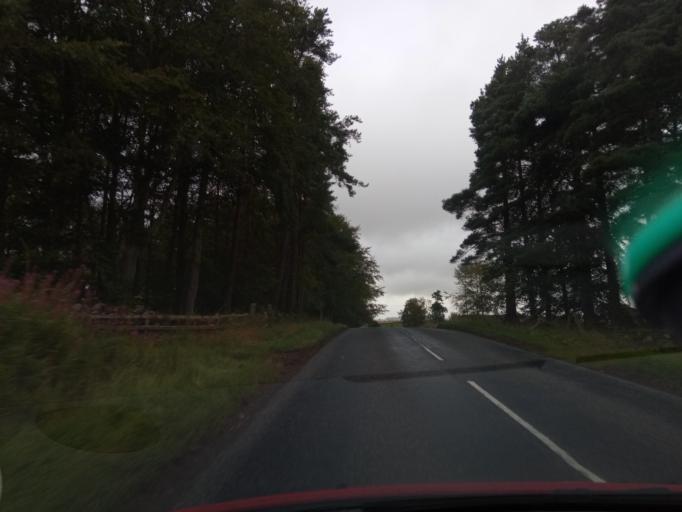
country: GB
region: Scotland
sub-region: The Scottish Borders
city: Earlston
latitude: 55.6638
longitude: -2.5520
